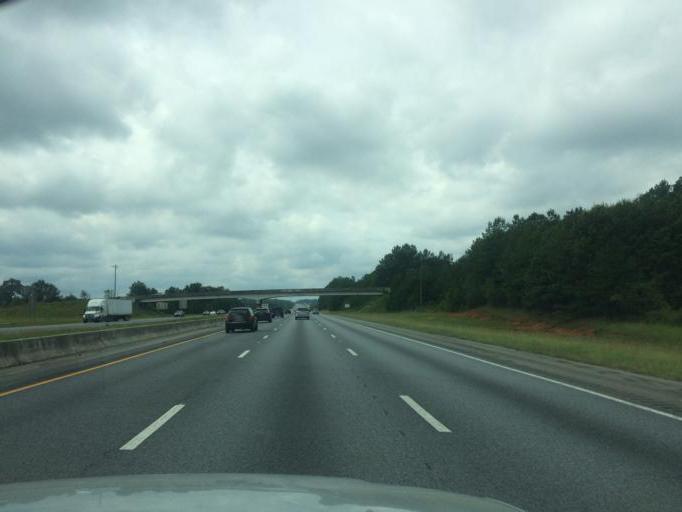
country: US
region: South Carolina
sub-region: Greenville County
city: Golden Grove
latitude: 34.7435
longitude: -82.4832
